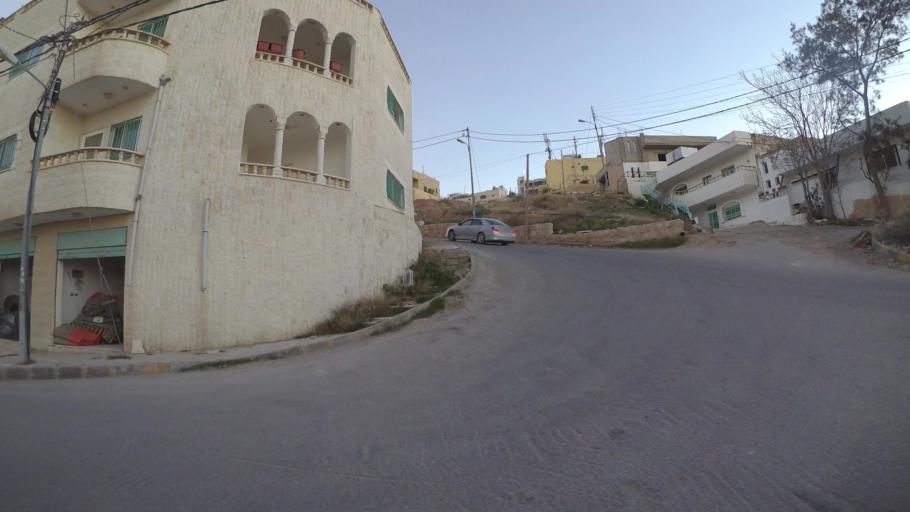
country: JO
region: Ma'an
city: Petra
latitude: 30.3207
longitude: 35.4727
